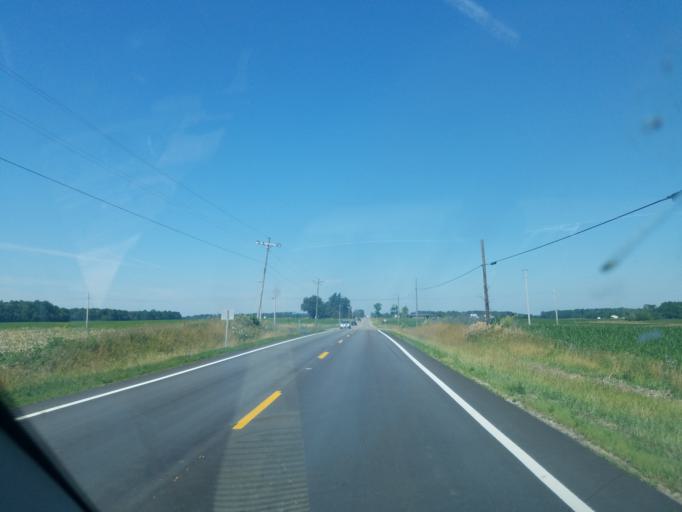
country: US
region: Ohio
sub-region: Shelby County
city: Botkins
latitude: 40.4389
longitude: -84.1344
